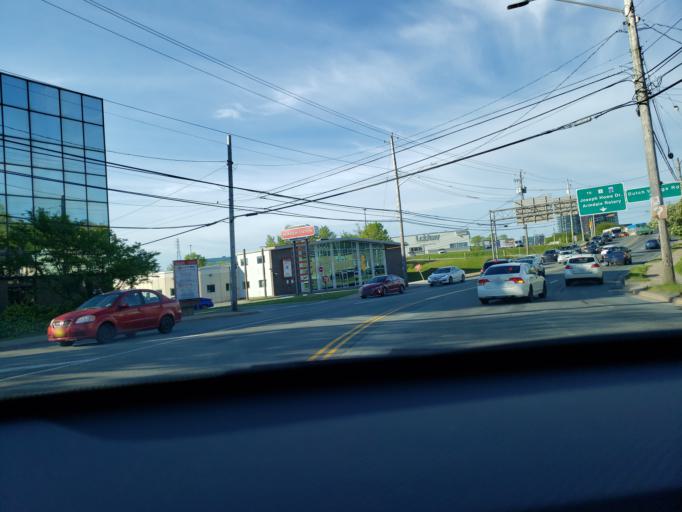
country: CA
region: Nova Scotia
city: Dartmouth
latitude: 44.6612
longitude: -63.6277
